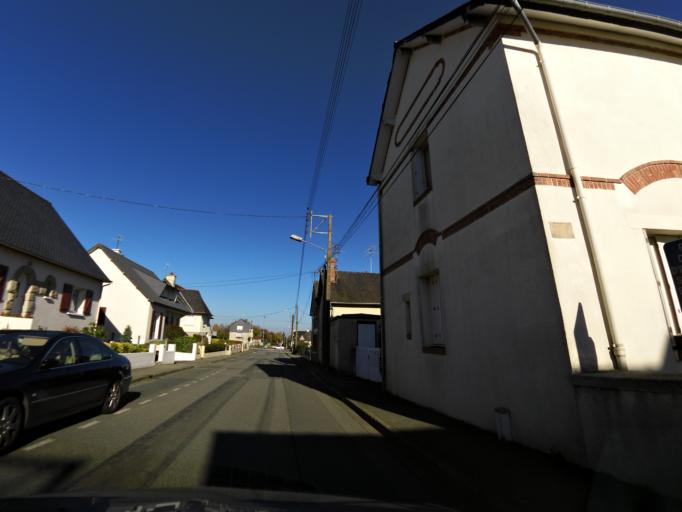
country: FR
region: Brittany
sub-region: Departement d'Ille-et-Vilaine
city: Bain-de-Bretagne
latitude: 47.8459
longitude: -1.6854
